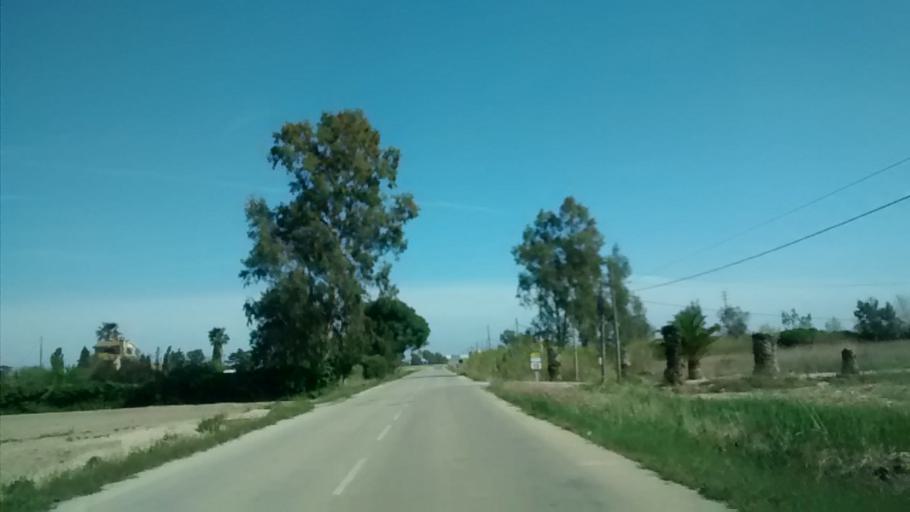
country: ES
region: Catalonia
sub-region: Provincia de Tarragona
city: Deltebre
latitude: 40.7129
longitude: 0.7530
